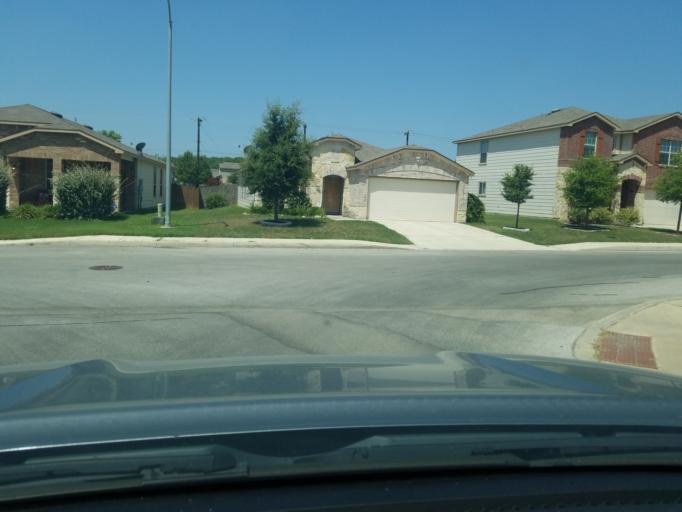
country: US
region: Texas
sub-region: Bexar County
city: Timberwood Park
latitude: 29.7043
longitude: -98.4814
